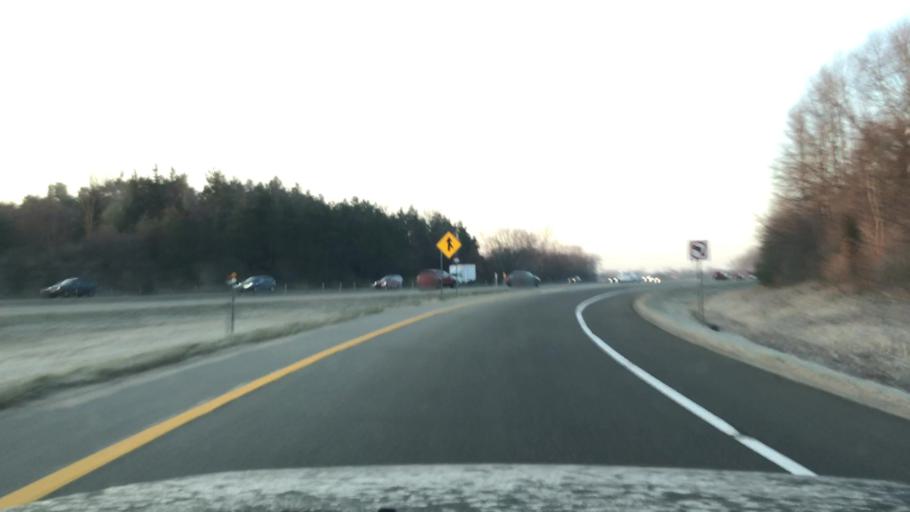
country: US
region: Michigan
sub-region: Kent County
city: East Grand Rapids
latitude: 42.9826
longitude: -85.6055
